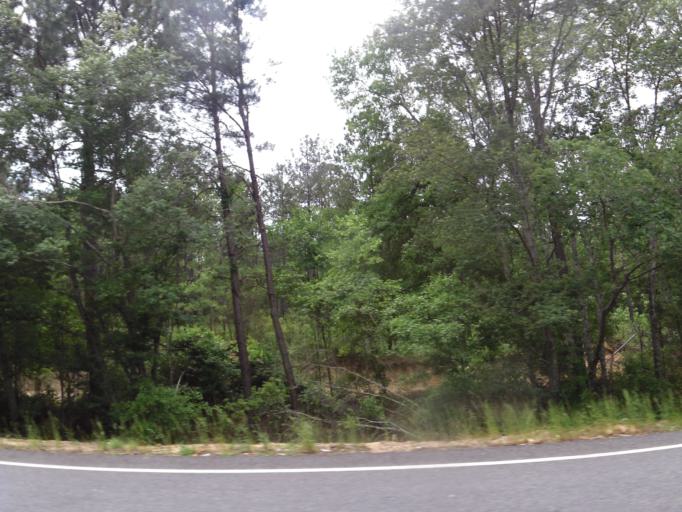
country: US
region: Georgia
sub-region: Candler County
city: Metter
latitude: 32.3892
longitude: -82.1758
